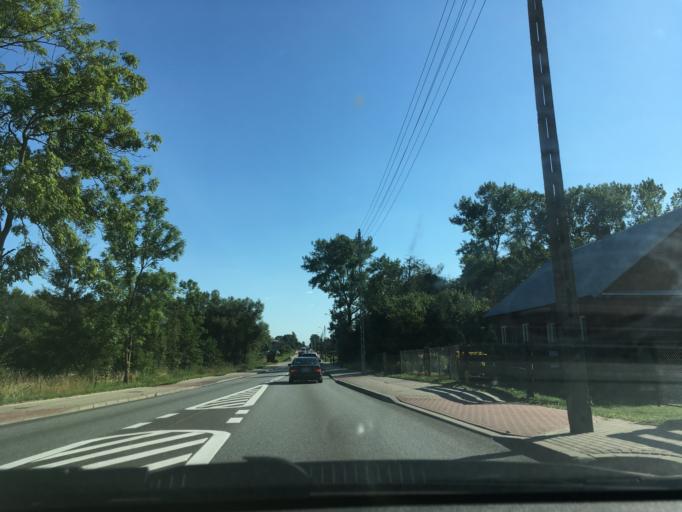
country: PL
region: Podlasie
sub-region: Powiat sokolski
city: Suchowola
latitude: 53.5068
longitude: 23.0987
